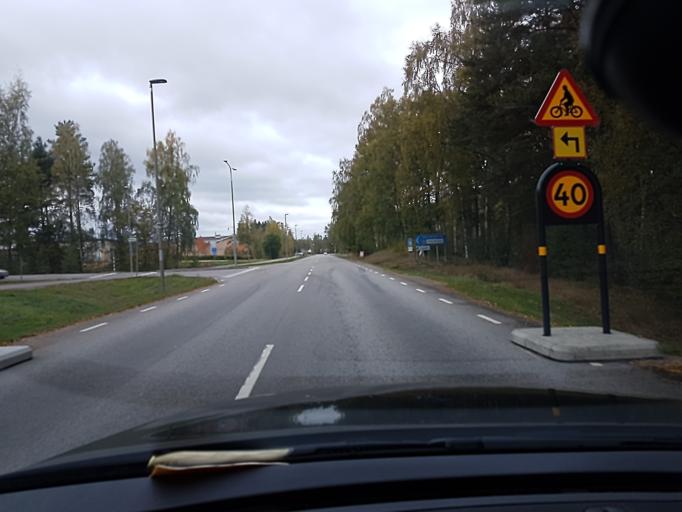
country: SE
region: Kronoberg
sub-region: Vaxjo Kommun
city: Vaexjoe
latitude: 56.9127
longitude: 14.8174
